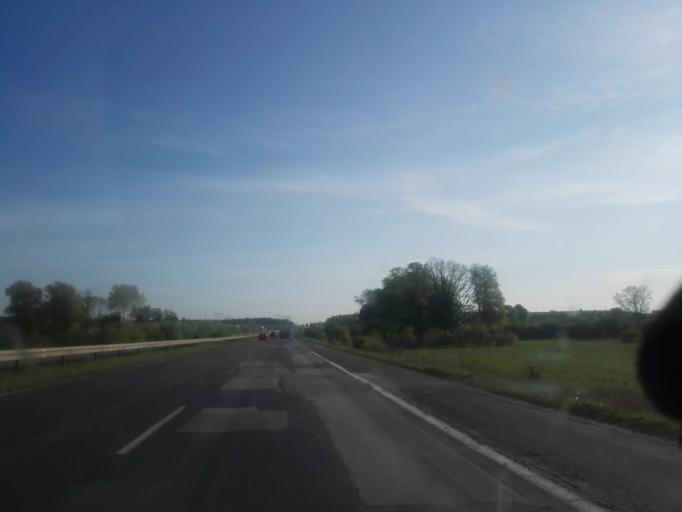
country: PL
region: Lodz Voivodeship
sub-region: Powiat radomszczanski
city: Radomsko
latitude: 51.1028
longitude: 19.3854
